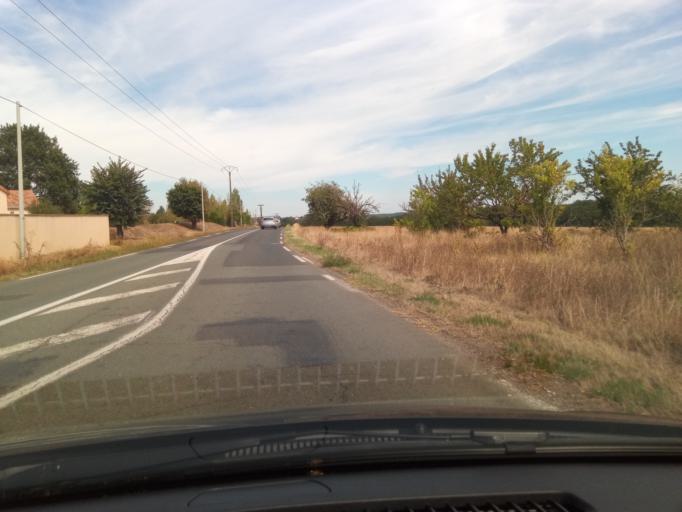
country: FR
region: Poitou-Charentes
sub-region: Departement de la Vienne
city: Chauvigny
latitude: 46.5569
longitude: 0.6134
